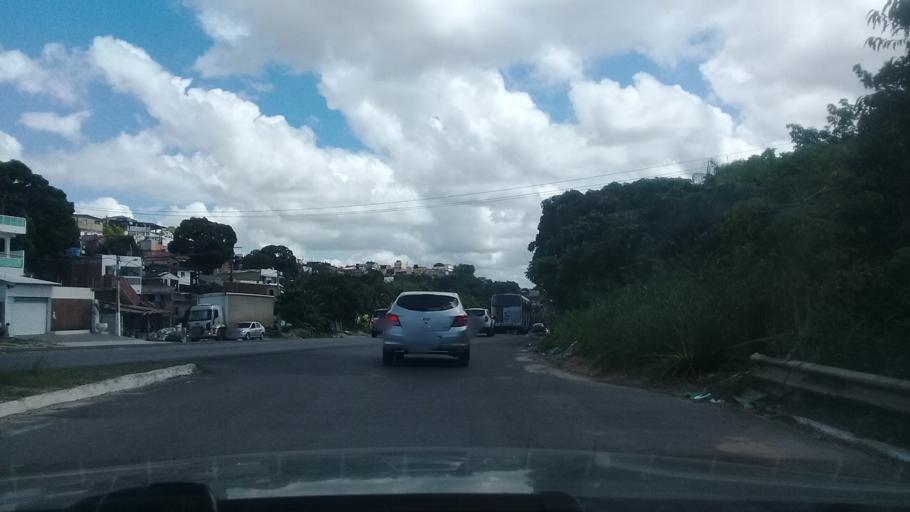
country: BR
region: Pernambuco
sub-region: Jaboatao Dos Guararapes
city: Jaboatao dos Guararapes
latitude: -8.1159
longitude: -34.9441
